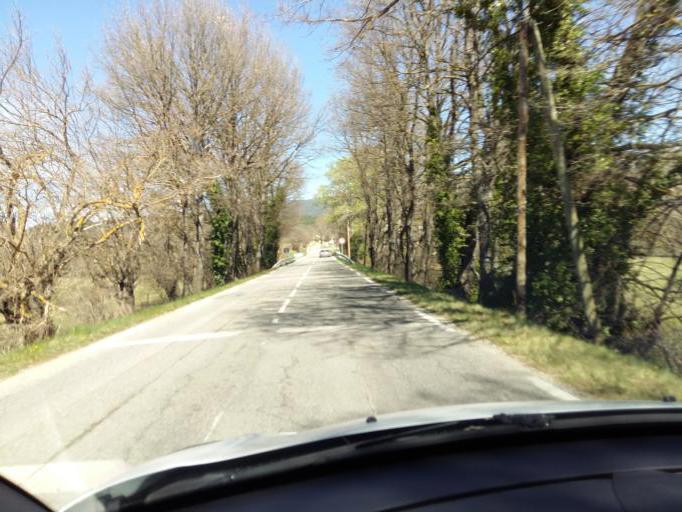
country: FR
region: Provence-Alpes-Cote d'Azur
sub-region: Departement du Vaucluse
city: Apt
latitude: 43.9043
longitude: 5.4358
